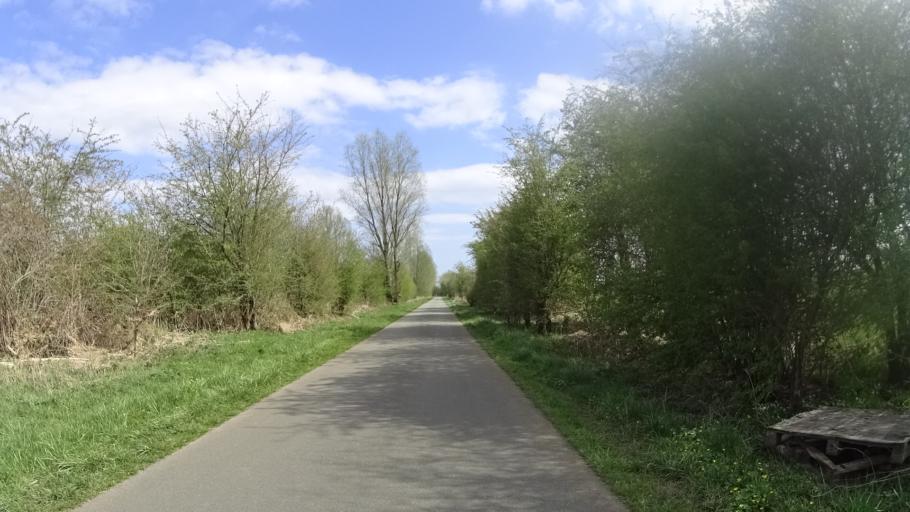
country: DE
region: Lower Saxony
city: Rhede
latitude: 53.0565
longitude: 7.2988
